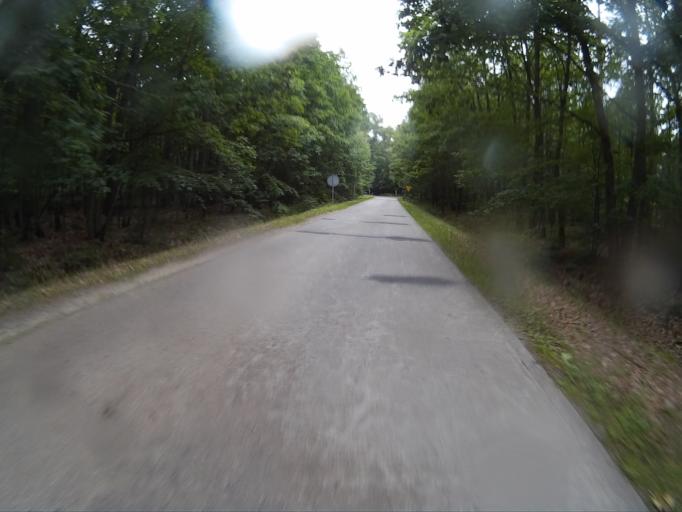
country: PL
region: Kujawsko-Pomorskie
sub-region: Powiat tucholski
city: Tuchola
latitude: 53.5499
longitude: 17.8663
